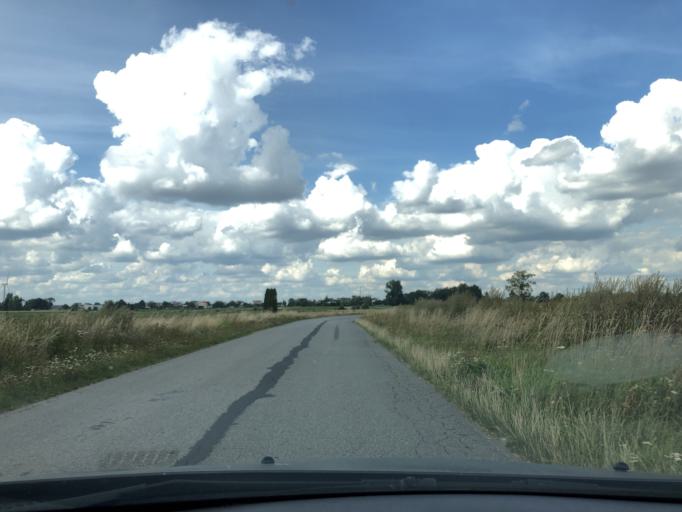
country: PL
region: Lodz Voivodeship
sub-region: Powiat wieruszowski
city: Walichnowy
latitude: 51.2540
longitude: 18.3903
